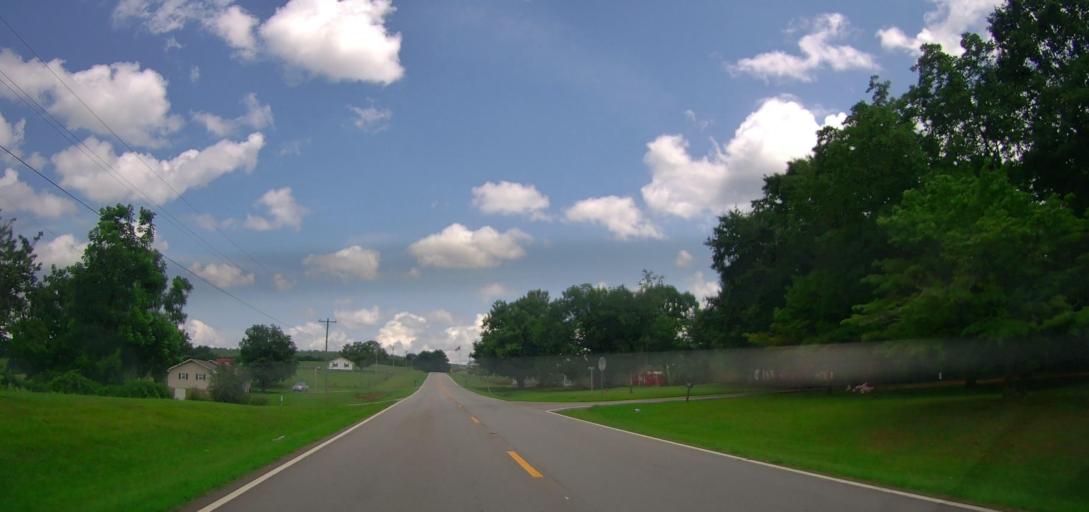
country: US
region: Georgia
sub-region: Carroll County
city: Bowdon
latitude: 33.4457
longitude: -85.2857
